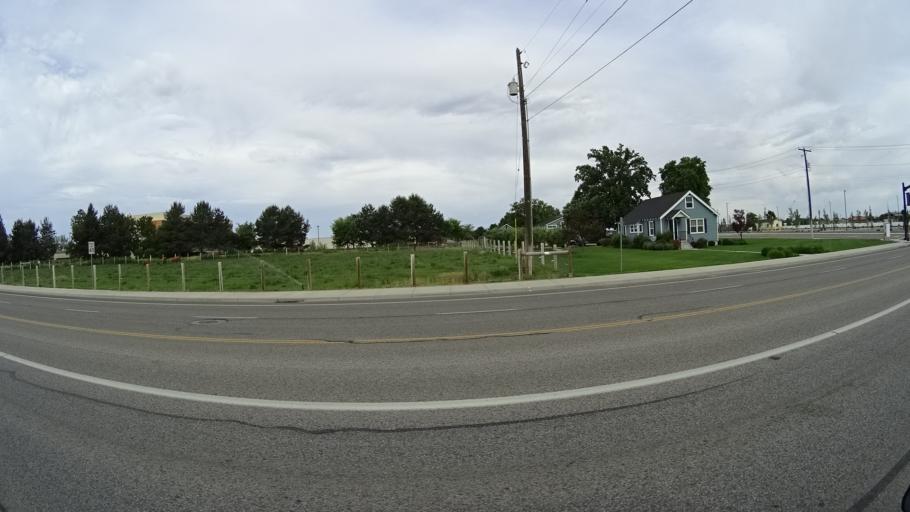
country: US
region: Idaho
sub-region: Ada County
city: Meridian
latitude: 43.5957
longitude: -116.3744
